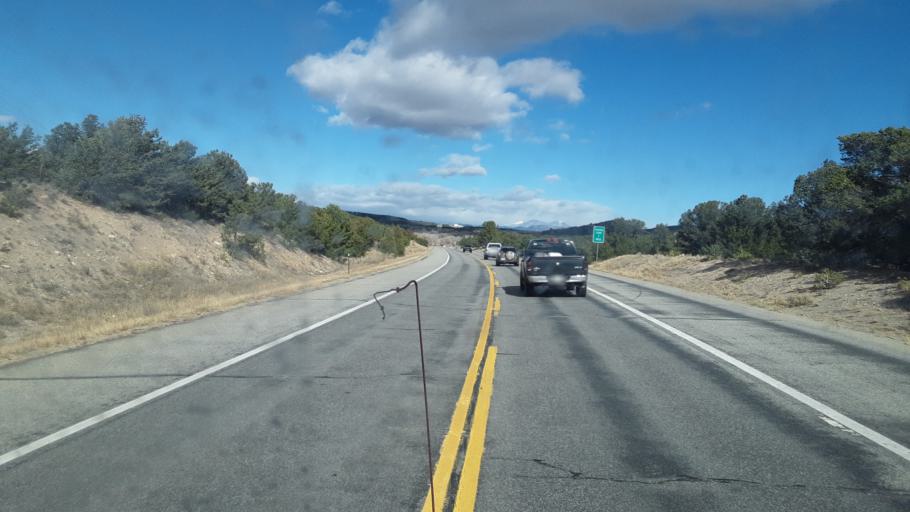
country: US
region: Colorado
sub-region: Chaffee County
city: Salida
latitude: 38.6261
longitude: -106.0775
